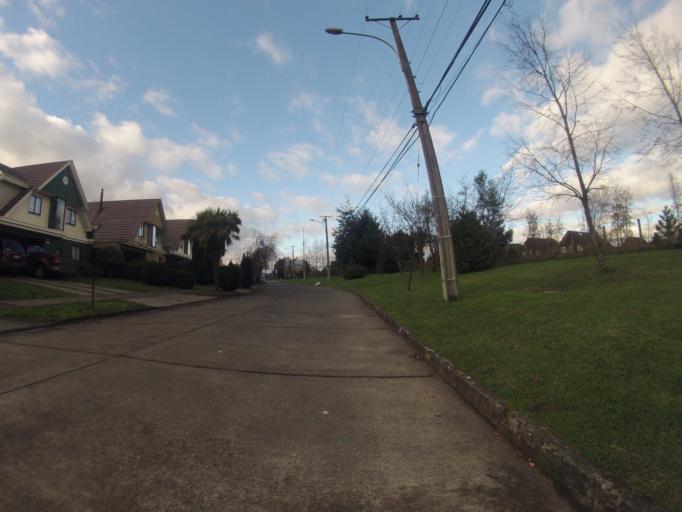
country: CL
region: Araucania
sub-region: Provincia de Cautin
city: Temuco
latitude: -38.7364
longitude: -72.6455
